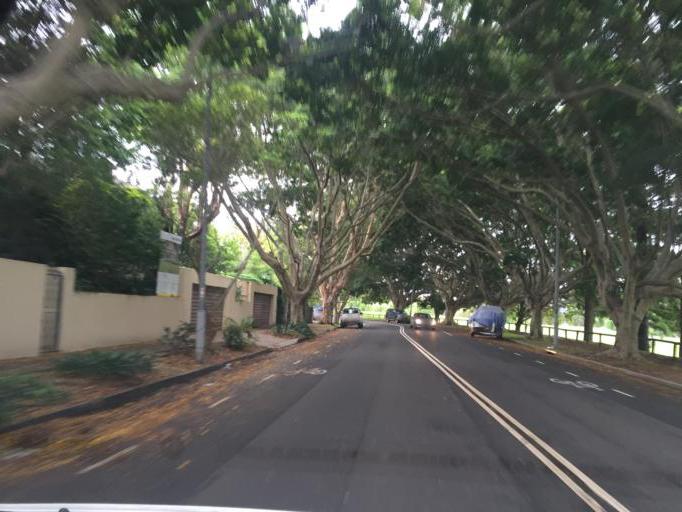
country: AU
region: New South Wales
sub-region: Woollahra
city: Bellevue Hill
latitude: -33.8776
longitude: 151.2618
